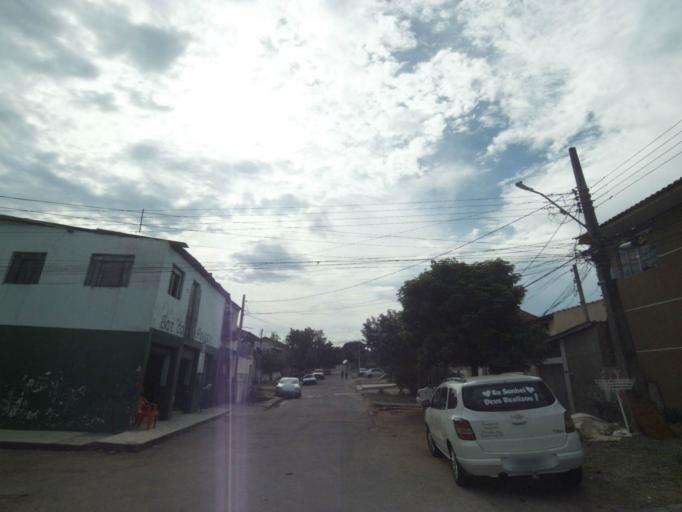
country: BR
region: Parana
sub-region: Pinhais
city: Pinhais
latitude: -25.4454
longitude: -49.2169
